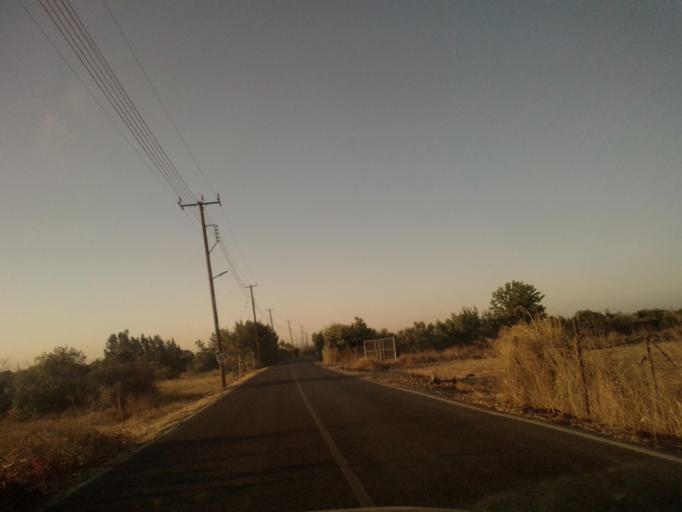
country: CY
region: Limassol
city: Ypsonas
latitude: 34.6770
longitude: 32.9572
